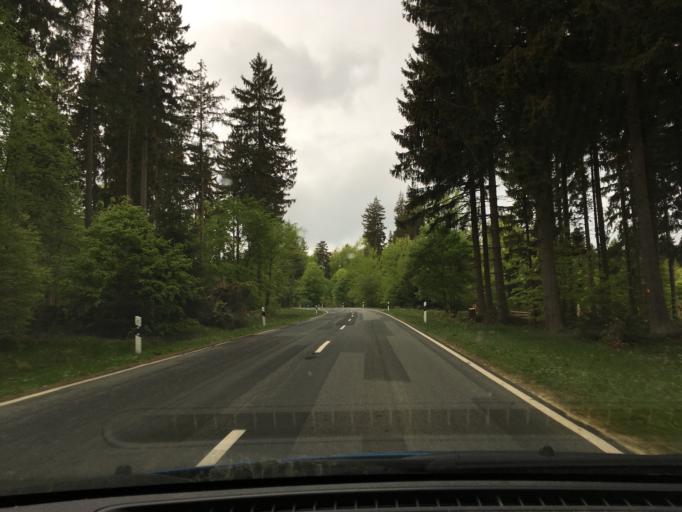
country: DE
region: Lower Saxony
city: Heinade
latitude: 51.7956
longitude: 9.6251
